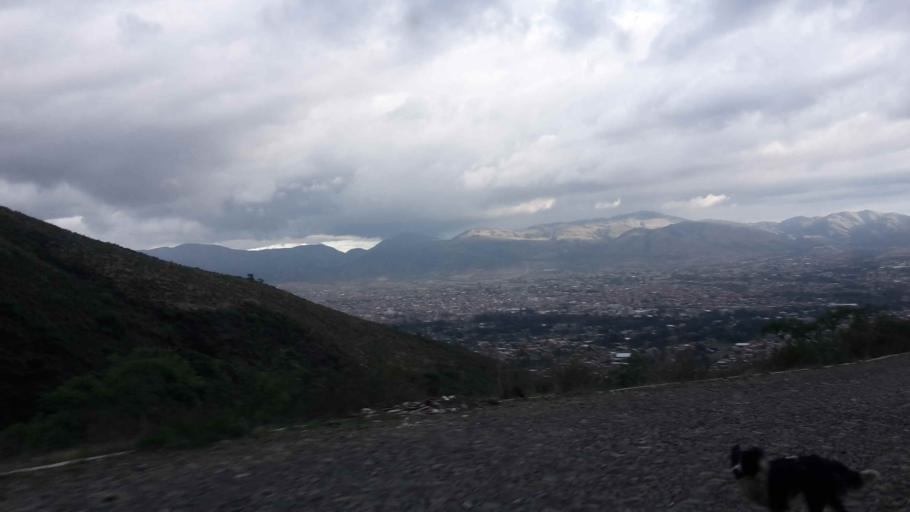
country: BO
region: Cochabamba
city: Cochabamba
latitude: -17.3671
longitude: -66.0613
